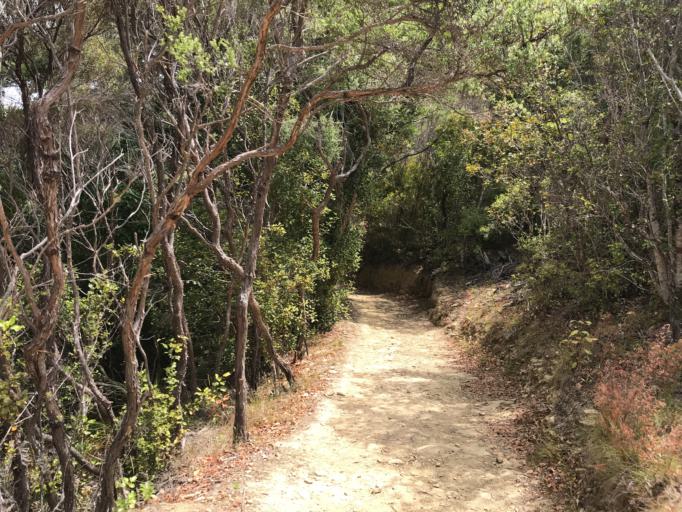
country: NZ
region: Marlborough
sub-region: Marlborough District
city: Picton
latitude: -41.1216
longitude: 174.1905
